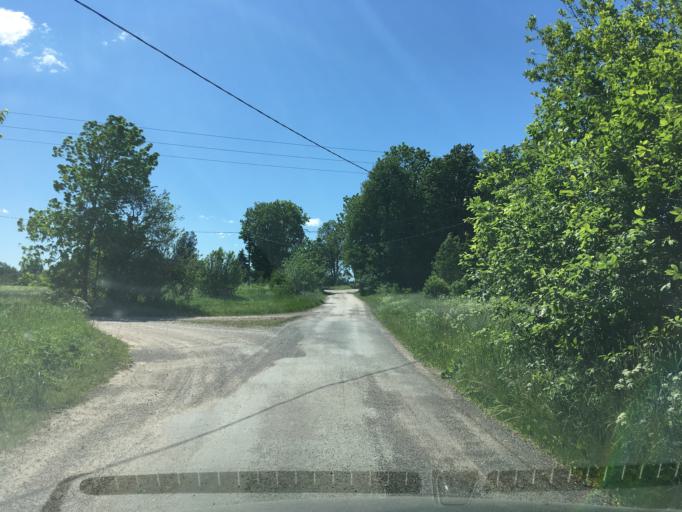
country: EE
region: Harju
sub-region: Rae vald
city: Vaida
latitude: 59.1587
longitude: 25.1266
